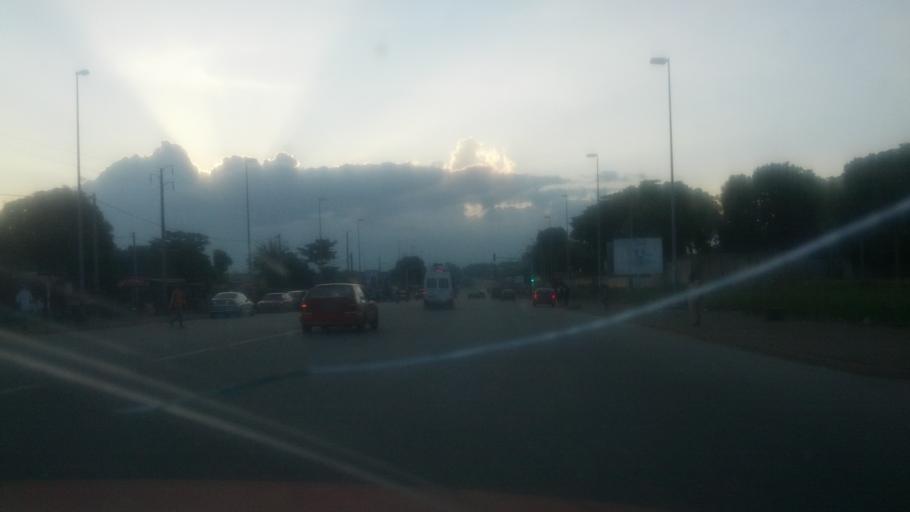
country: CI
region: Vallee du Bandama
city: Bouake
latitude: 7.6856
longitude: -5.0501
